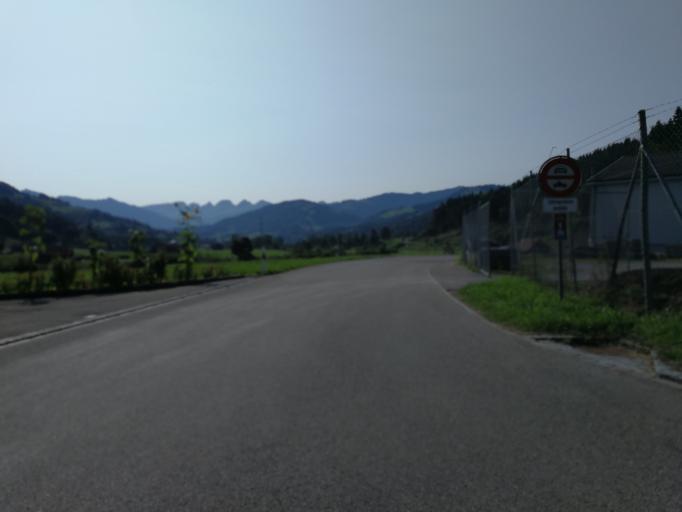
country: CH
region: Saint Gallen
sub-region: Wahlkreis Toggenburg
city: Wattwil
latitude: 47.2852
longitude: 9.0937
